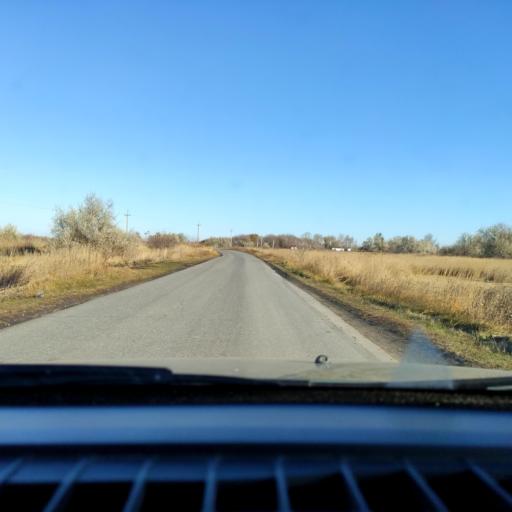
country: RU
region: Samara
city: Tol'yatti
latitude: 53.6564
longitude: 49.3313
